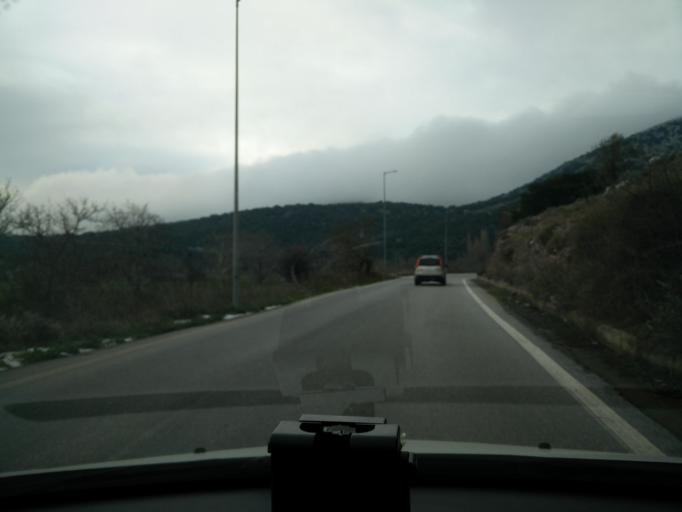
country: GR
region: Crete
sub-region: Nomos Irakleiou
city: Malia
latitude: 35.2022
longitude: 25.4805
